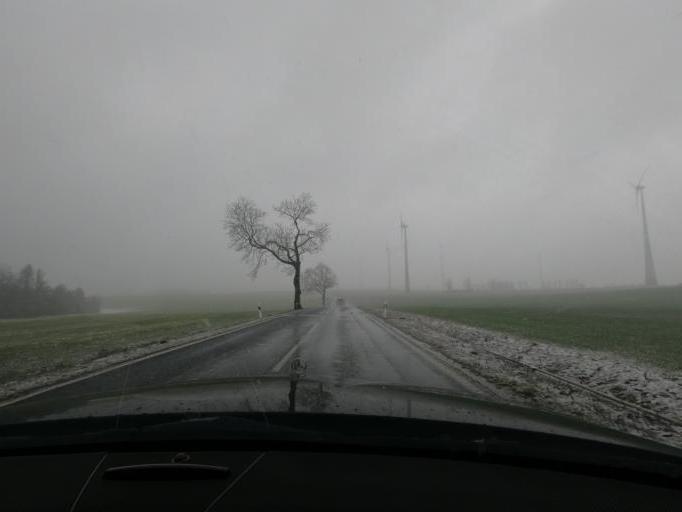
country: DE
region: Thuringia
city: Buttstedt
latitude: 51.2496
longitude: 10.2760
